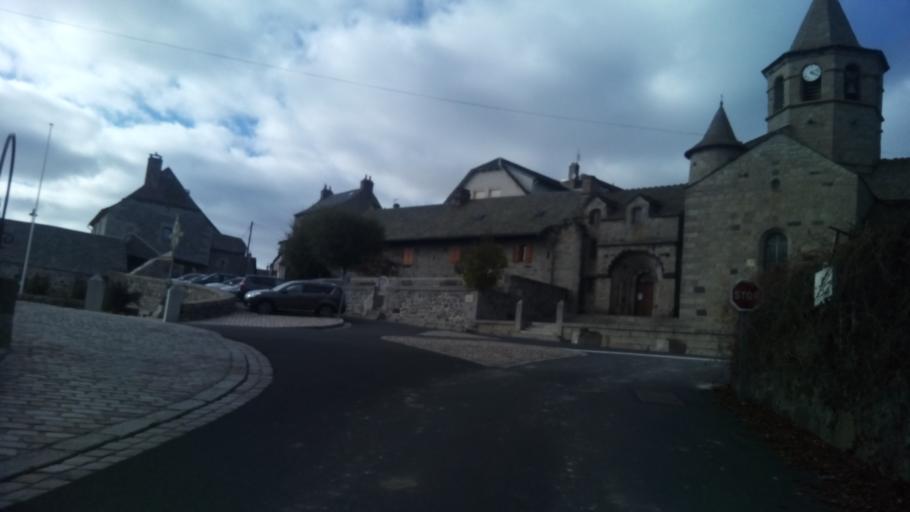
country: FR
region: Auvergne
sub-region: Departement du Cantal
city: Chaudes-Aigues
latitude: 44.6620
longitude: 3.0468
